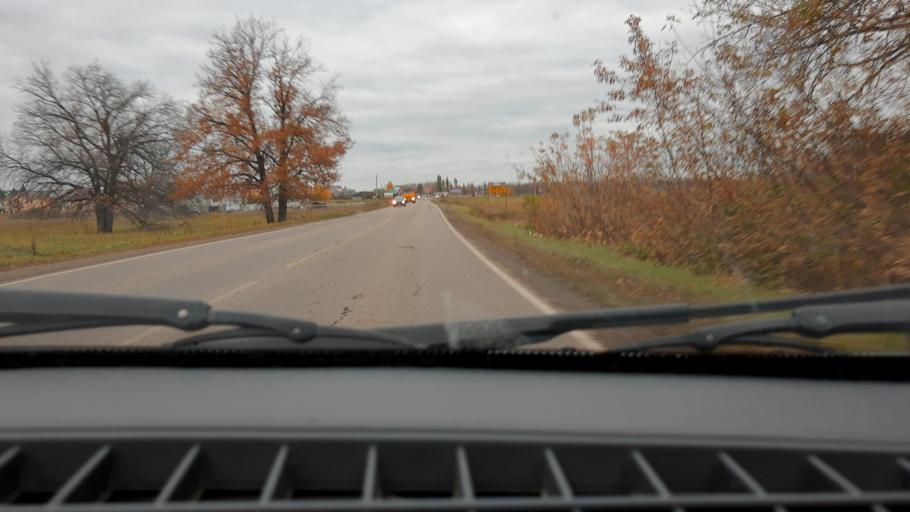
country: RU
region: Bashkortostan
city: Ufa
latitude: 54.5661
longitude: 55.9628
